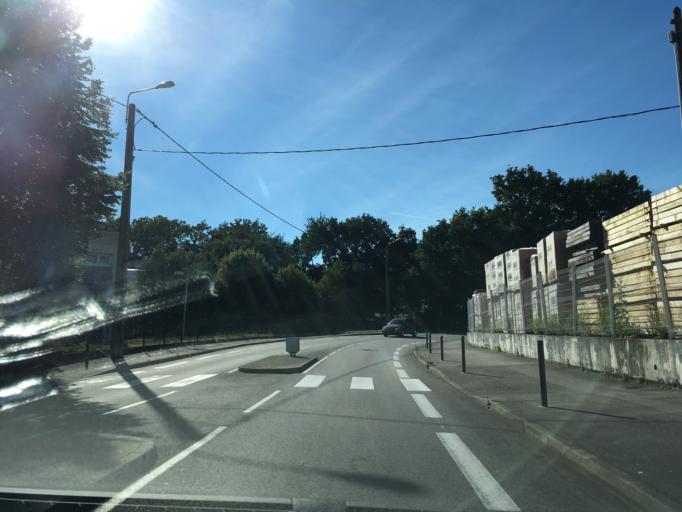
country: FR
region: Brittany
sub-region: Departement du Finistere
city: Quimper
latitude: 47.9964
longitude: -4.0833
